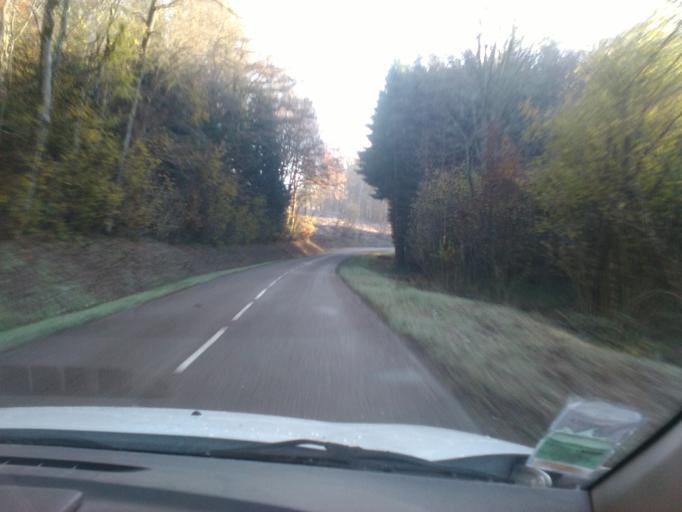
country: FR
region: Lorraine
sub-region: Departement des Vosges
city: Uzemain
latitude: 48.0571
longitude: 6.3554
